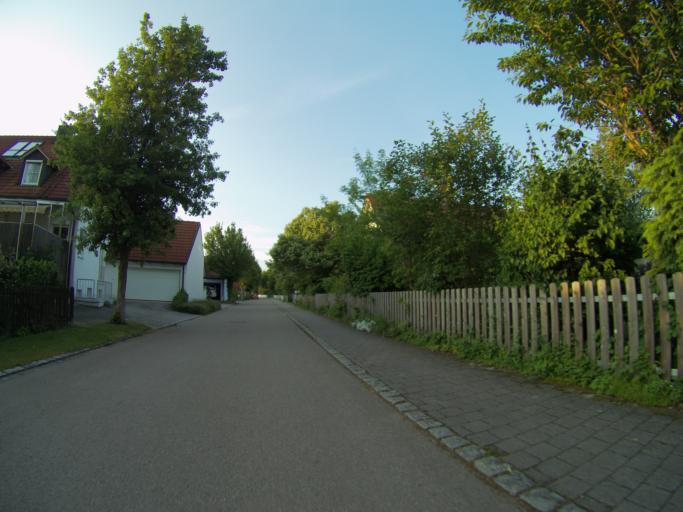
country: DE
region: Bavaria
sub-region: Upper Bavaria
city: Marzling
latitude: 48.4059
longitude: 11.7942
